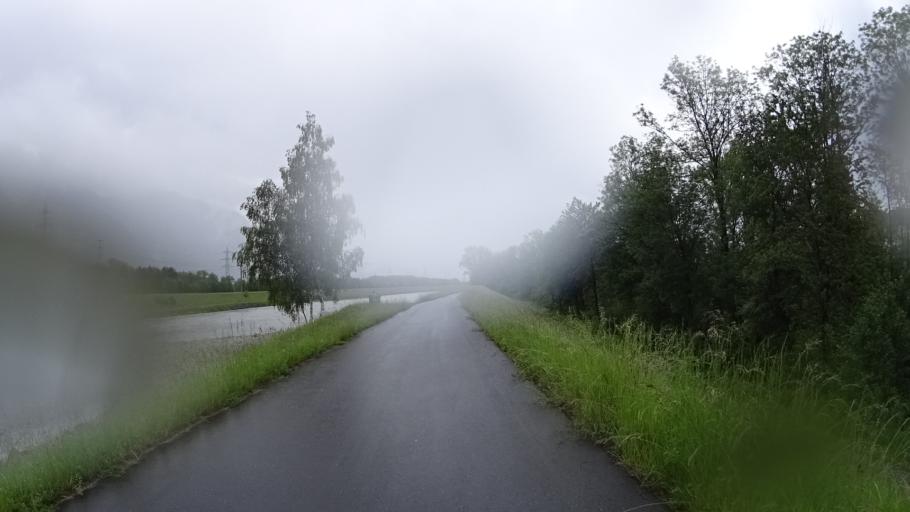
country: LI
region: Gamprin
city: Gamprin
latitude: 47.2203
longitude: 9.5027
